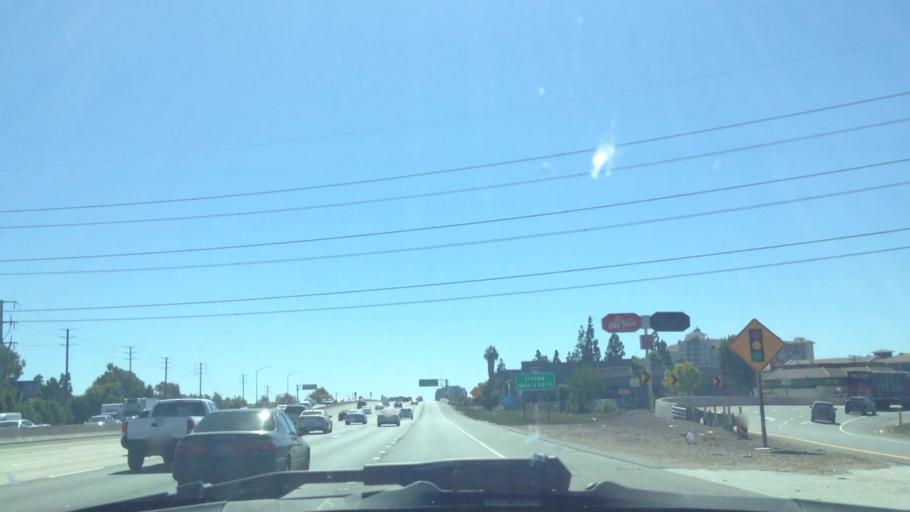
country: US
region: California
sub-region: Orange County
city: Santa Ana
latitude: 33.7118
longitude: -117.8491
